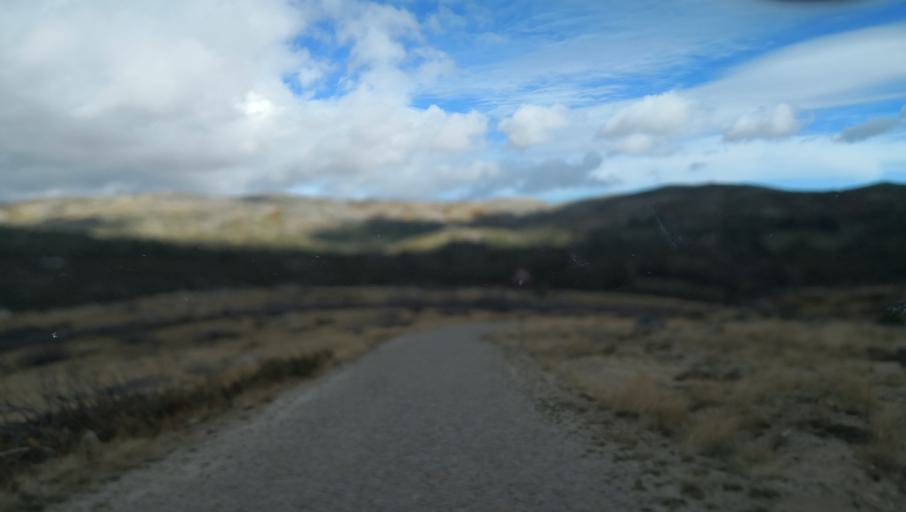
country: PT
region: Vila Real
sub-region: Vila Real
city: Vila Real
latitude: 41.3738
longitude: -7.8118
